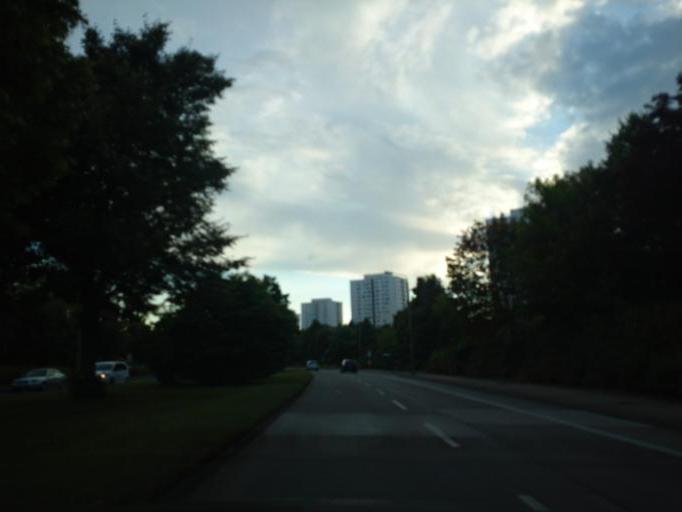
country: DE
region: Berlin
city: Marzahn
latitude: 52.5451
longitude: 13.5590
